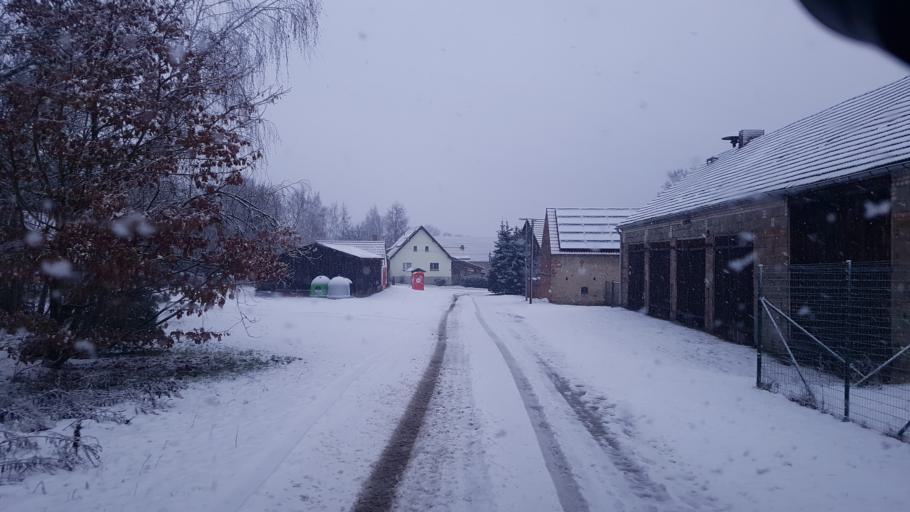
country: DE
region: Brandenburg
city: Schenkendobern
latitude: 51.9075
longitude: 14.5766
